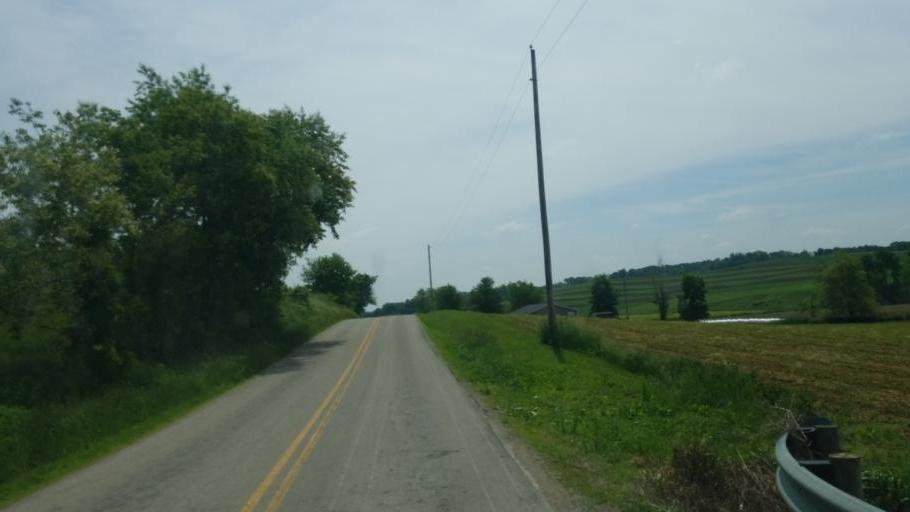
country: US
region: Ohio
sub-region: Tuscarawas County
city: Sugarcreek
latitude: 40.5031
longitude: -81.6745
